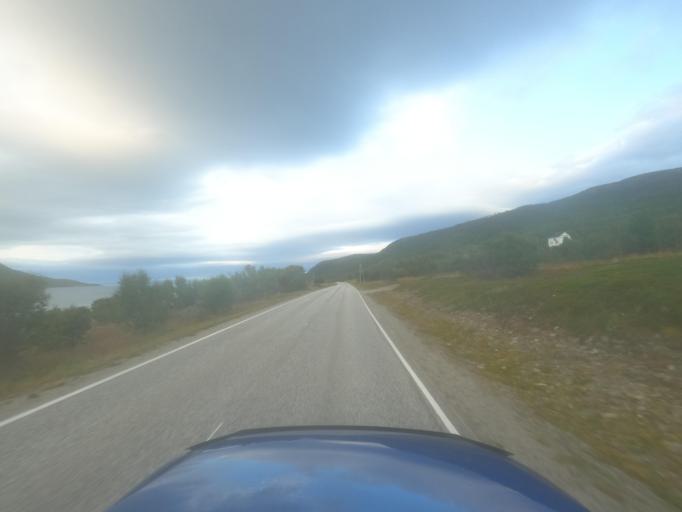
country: NO
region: Finnmark Fylke
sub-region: Porsanger
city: Lakselv
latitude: 70.4740
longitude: 25.1277
